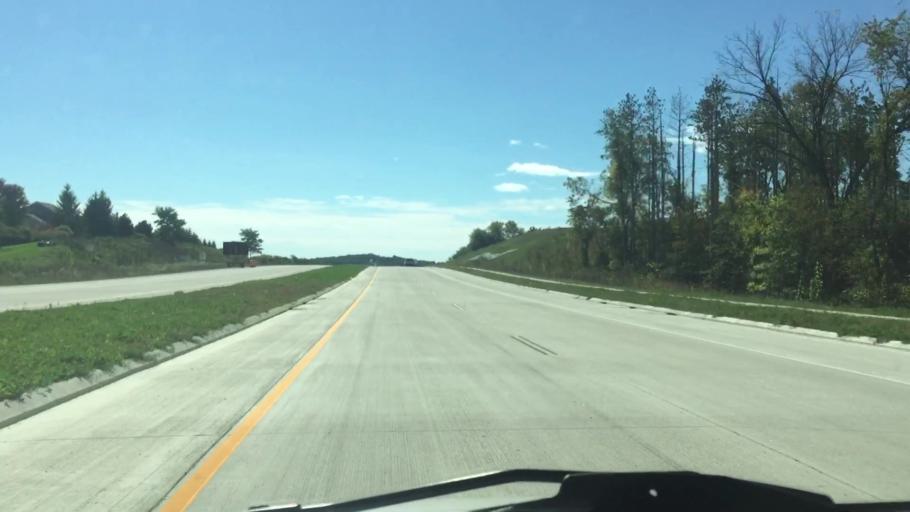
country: US
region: Wisconsin
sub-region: Waukesha County
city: Pewaukee
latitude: 43.0316
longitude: -88.2858
